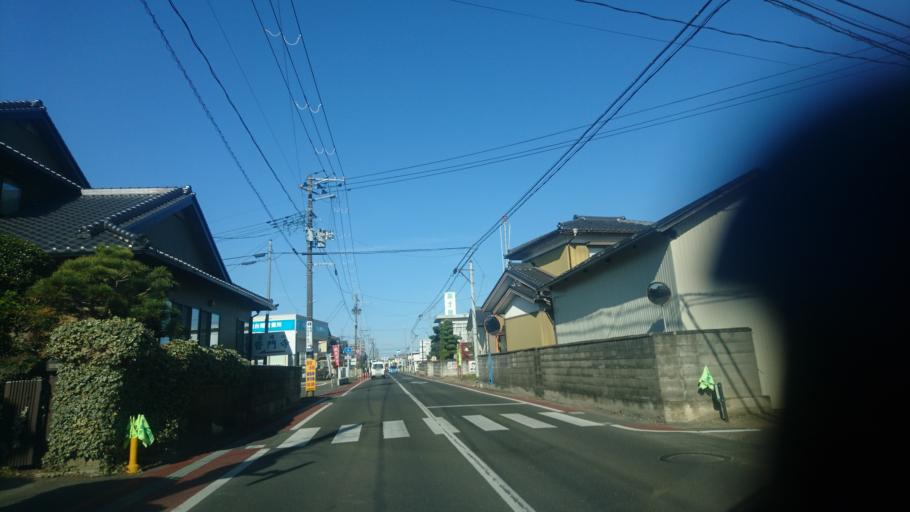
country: JP
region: Miyagi
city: Sendai
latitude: 38.1868
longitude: 140.8855
